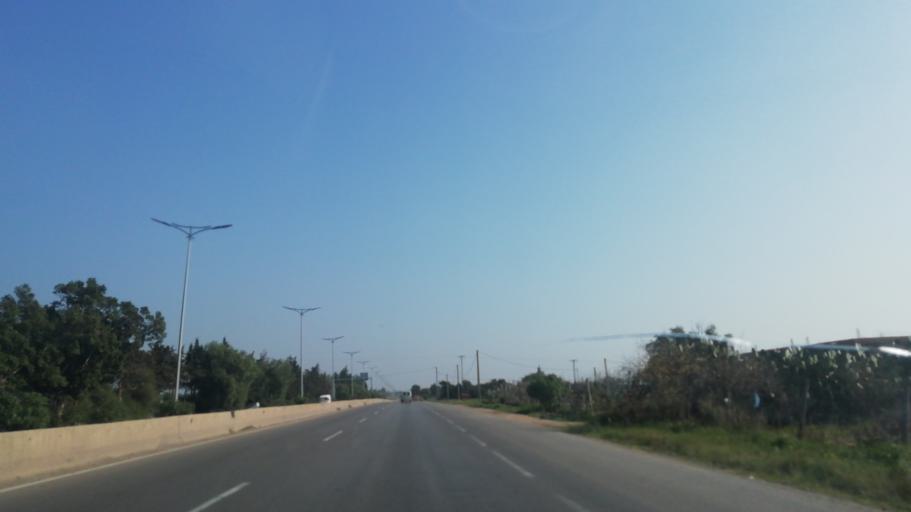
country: DZ
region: Oran
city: Bou Tlelis
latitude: 35.5728
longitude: -0.8758
